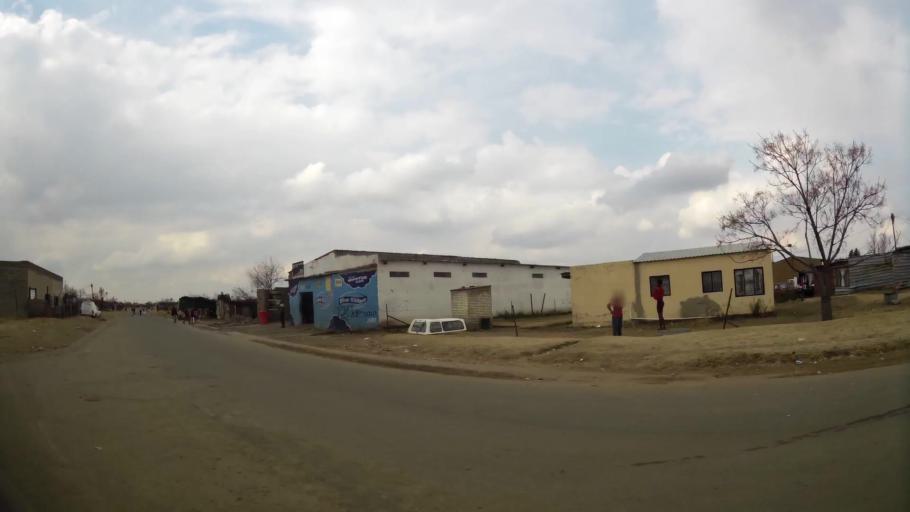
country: ZA
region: Orange Free State
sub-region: Fezile Dabi District Municipality
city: Sasolburg
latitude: -26.8604
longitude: 27.8819
